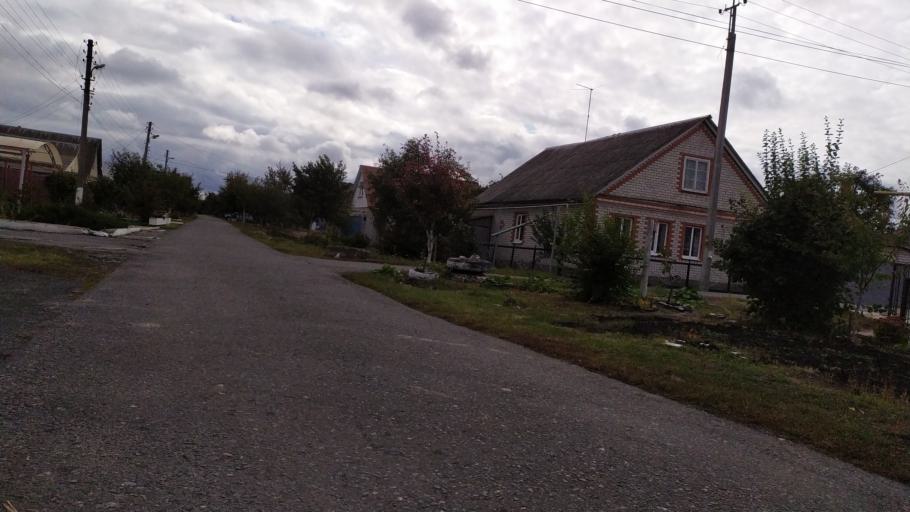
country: RU
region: Kursk
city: Kursk
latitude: 51.6457
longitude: 36.1517
